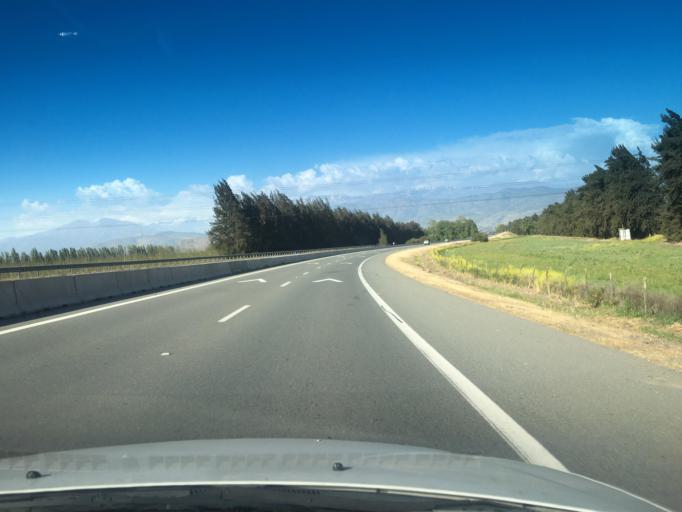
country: CL
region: Santiago Metropolitan
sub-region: Provincia de Chacabuco
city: Chicureo Abajo
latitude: -33.2949
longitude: -70.7199
